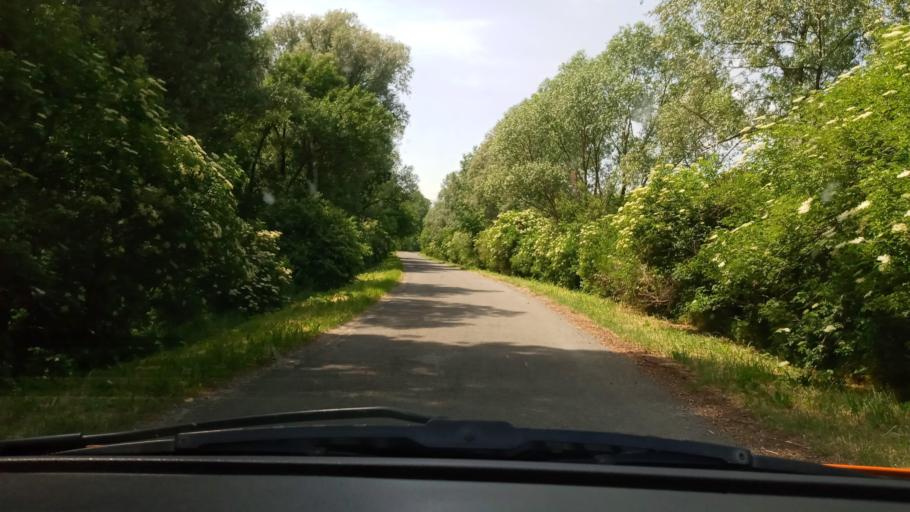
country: HU
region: Baranya
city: Sellye
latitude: 45.8076
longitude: 17.8780
